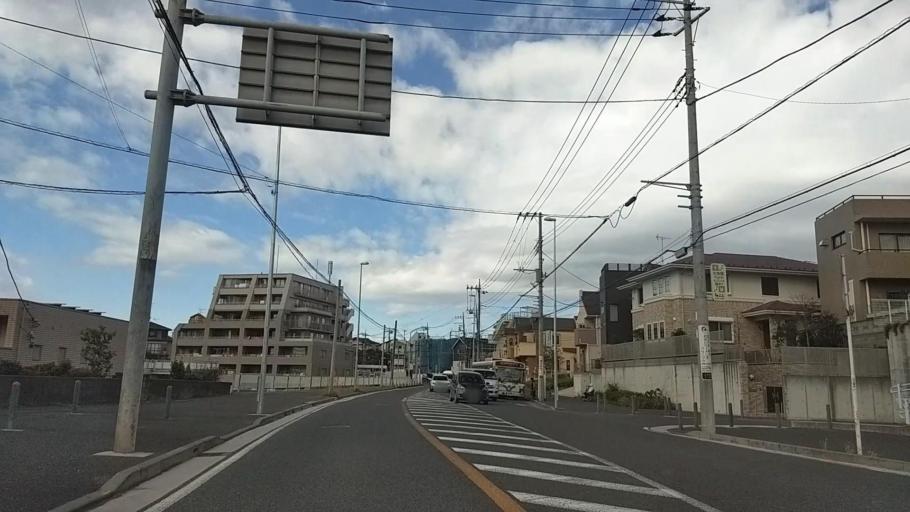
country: JP
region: Kanagawa
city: Yokohama
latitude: 35.5091
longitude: 139.6388
